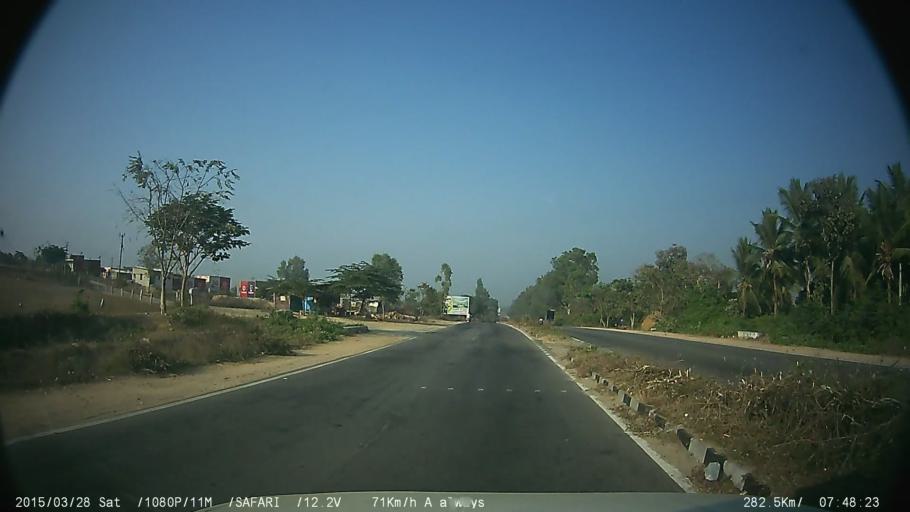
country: IN
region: Karnataka
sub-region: Mandya
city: Pandavapura
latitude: 12.4811
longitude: 76.7718
